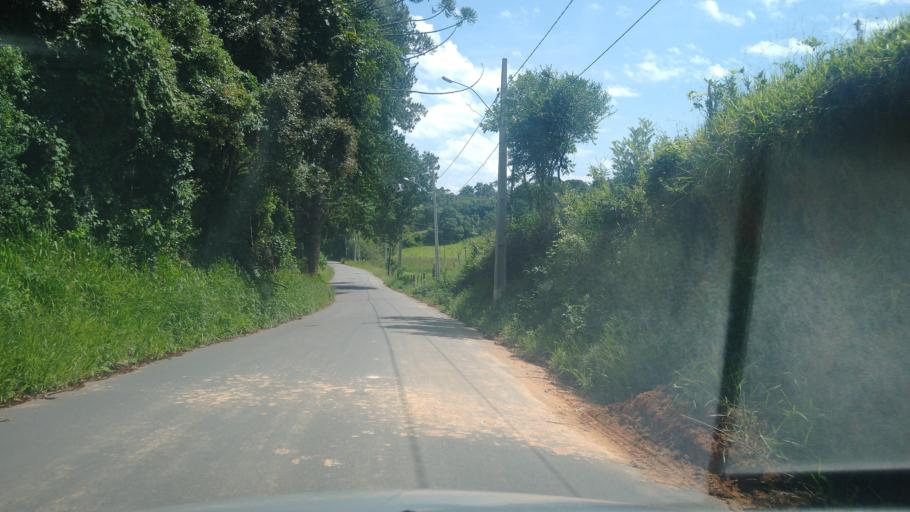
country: BR
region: Minas Gerais
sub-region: Extrema
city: Extrema
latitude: -22.7861
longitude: -46.2879
